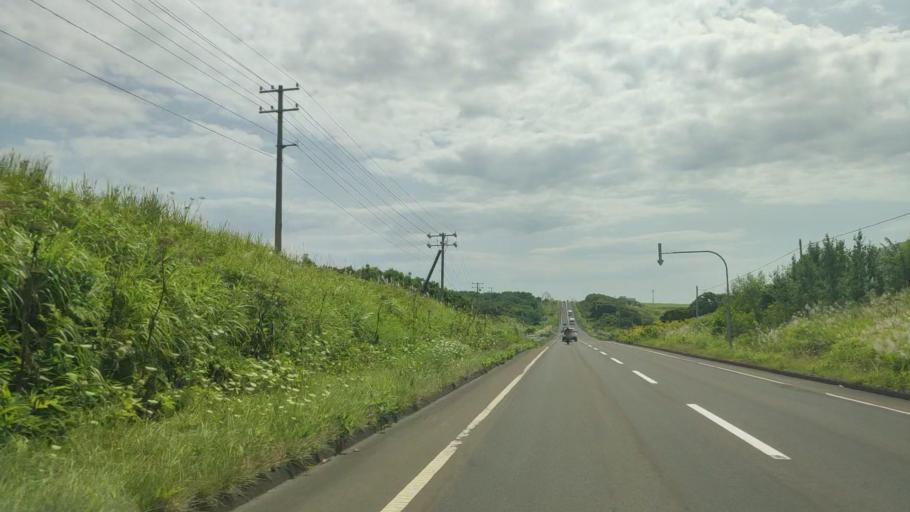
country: JP
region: Hokkaido
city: Rumoi
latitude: 44.4345
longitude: 141.7506
